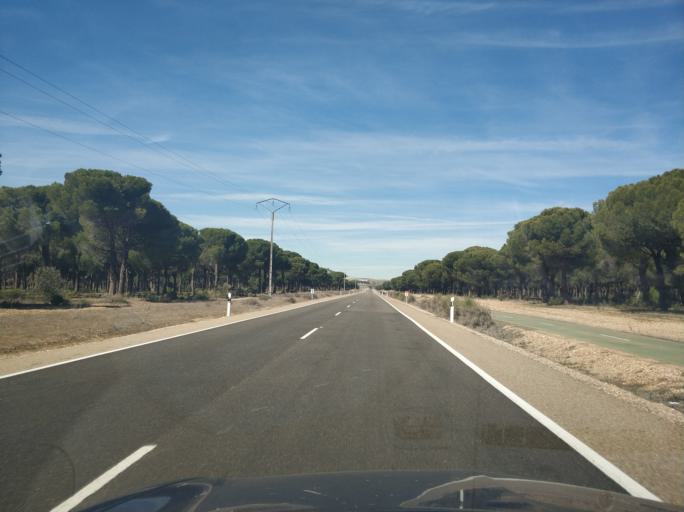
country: ES
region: Castille and Leon
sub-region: Provincia de Valladolid
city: Simancas
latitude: 41.5711
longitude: -4.8056
